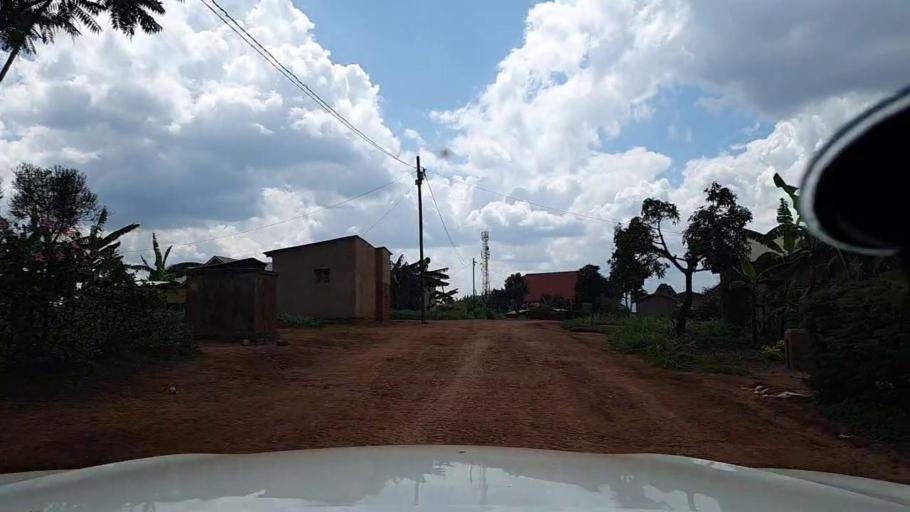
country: RW
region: Southern Province
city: Gitarama
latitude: -1.8377
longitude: 29.8318
